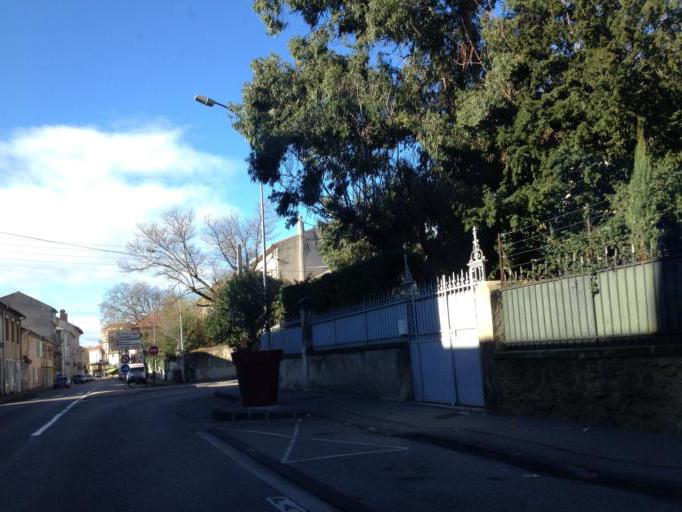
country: FR
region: Provence-Alpes-Cote d'Azur
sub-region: Departement du Vaucluse
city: Orange
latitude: 44.1376
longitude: 4.8146
